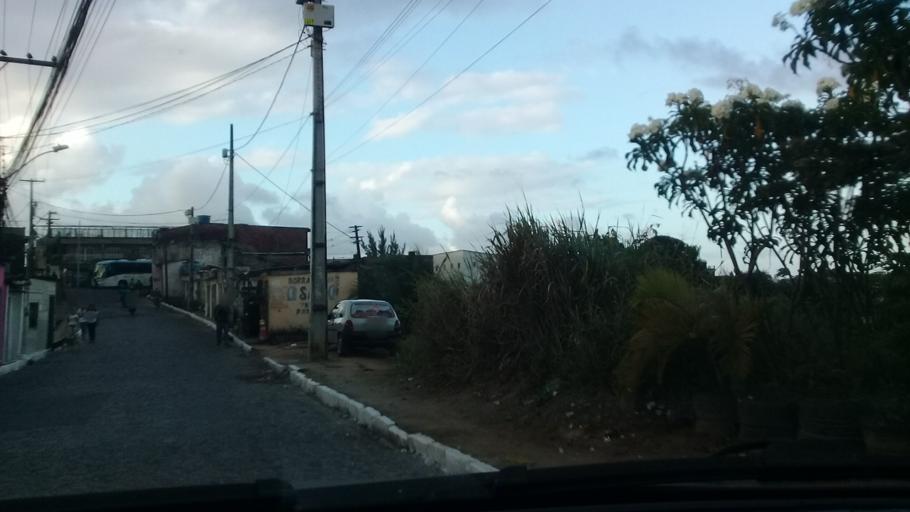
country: BR
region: Pernambuco
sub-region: Jaboatao Dos Guararapes
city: Jaboatao dos Guararapes
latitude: -8.1233
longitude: -34.9539
